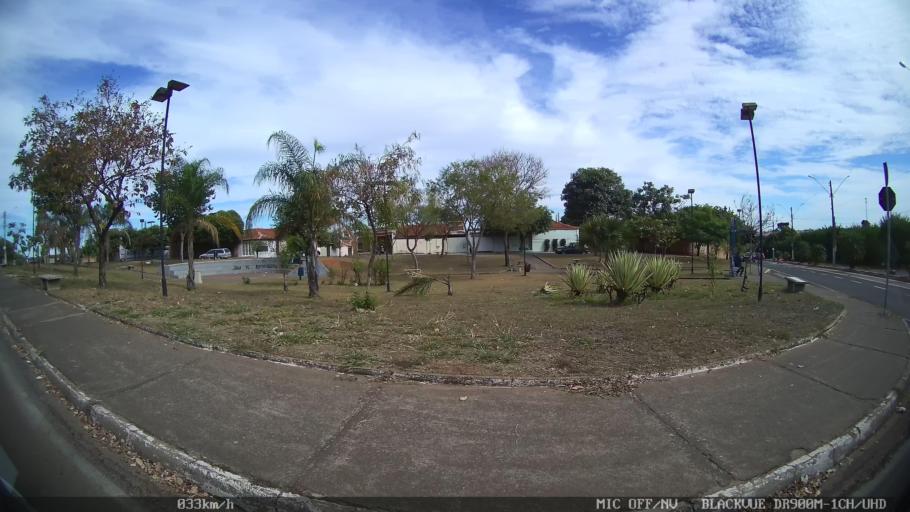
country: BR
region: Sao Paulo
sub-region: Catanduva
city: Catanduva
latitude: -21.1452
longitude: -48.9460
